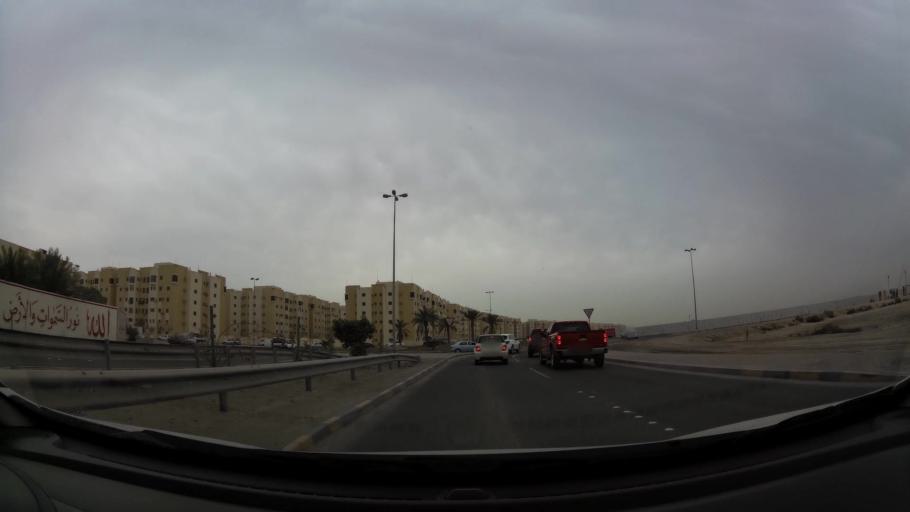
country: BH
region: Northern
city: Madinat `Isa
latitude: 26.1770
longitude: 50.5207
